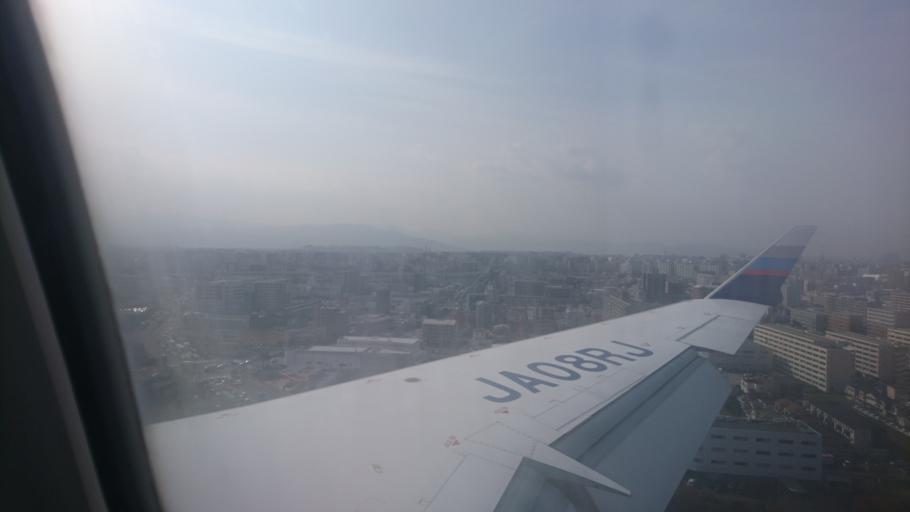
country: JP
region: Fukuoka
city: Fukuoka-shi
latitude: 33.6039
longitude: 130.4383
